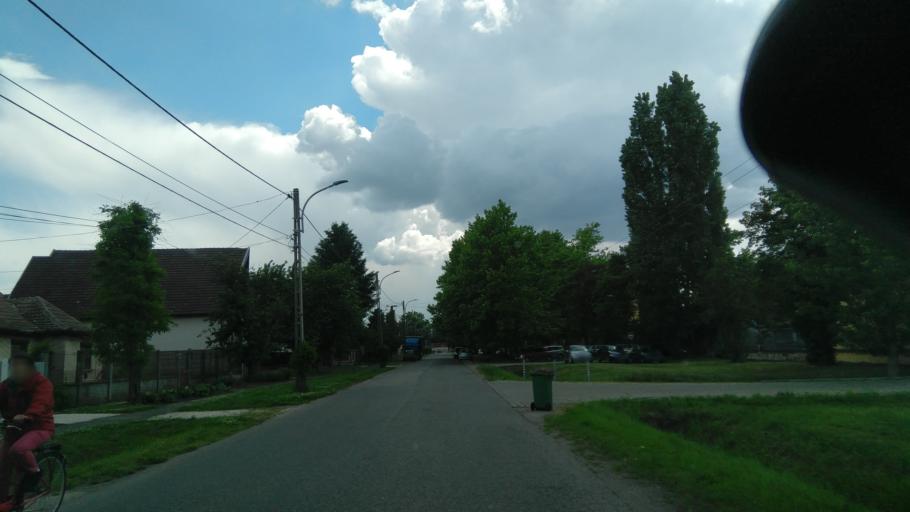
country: HU
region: Bekes
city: Gyula
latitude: 46.6602
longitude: 21.2695
